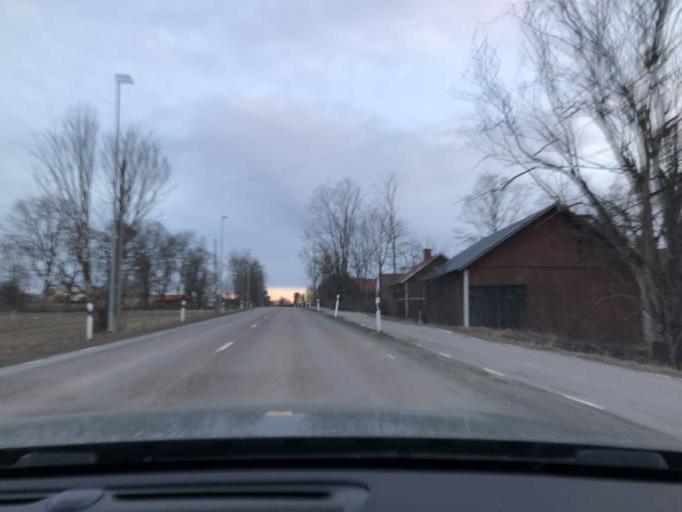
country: SE
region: Uppsala
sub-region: Uppsala Kommun
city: Gamla Uppsala
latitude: 59.9148
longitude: 17.6428
